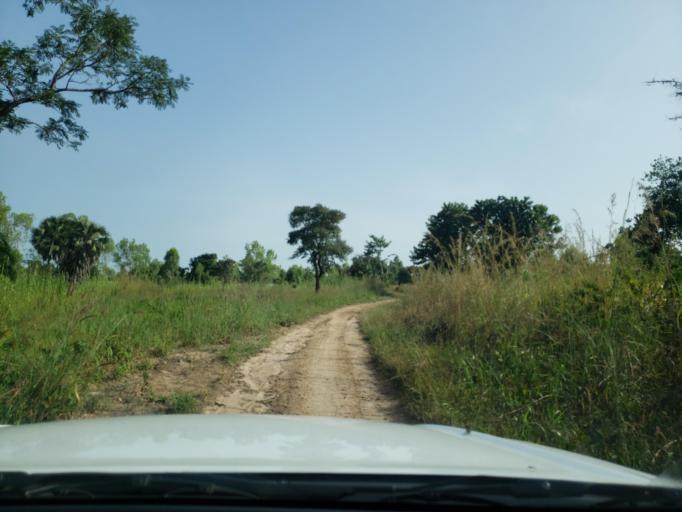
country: TG
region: Kara
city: Bafilo
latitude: 9.4087
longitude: 1.1754
